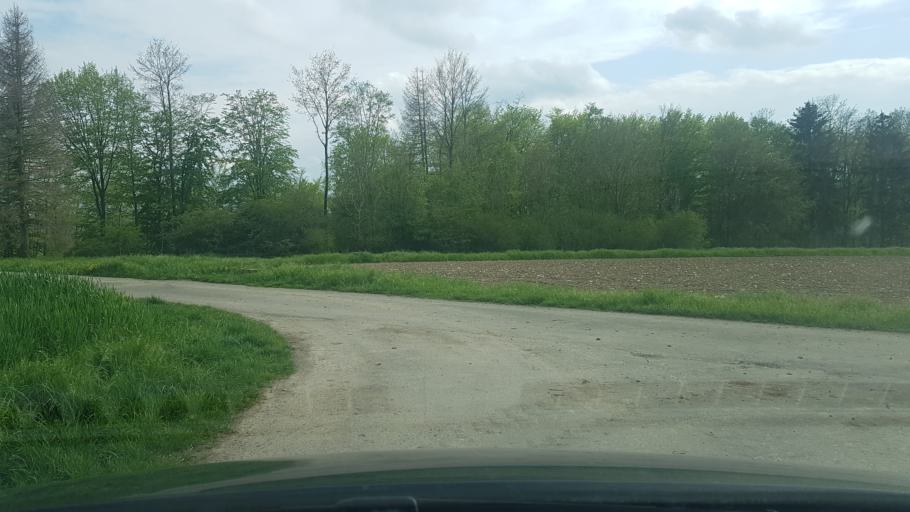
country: DE
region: North Rhine-Westphalia
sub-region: Regierungsbezirk Detmold
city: Paderborn
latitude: 51.6484
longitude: 8.7551
